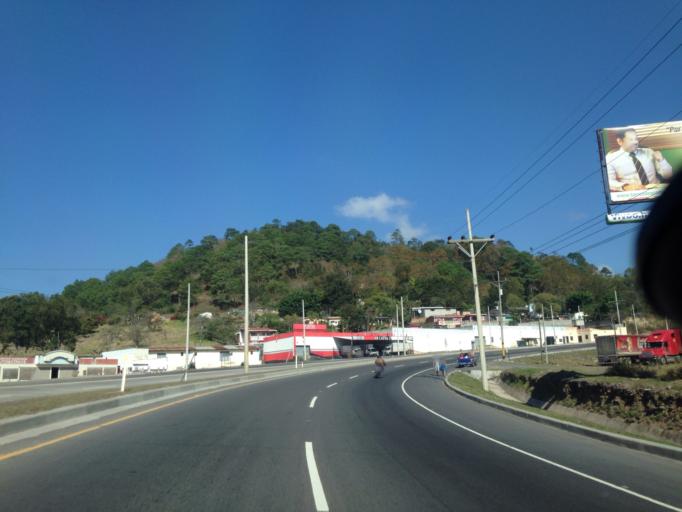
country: HN
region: Francisco Morazan
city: El Lolo
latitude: 14.1373
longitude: -87.2818
